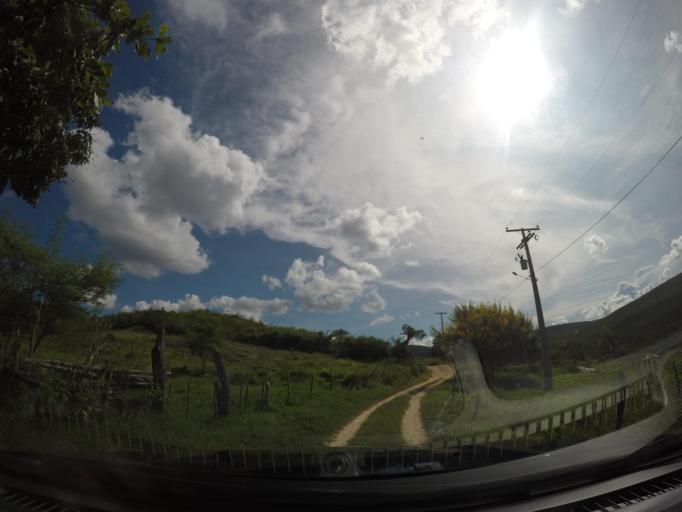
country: BR
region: Bahia
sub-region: Barra Da Estiva
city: Barra da Estiva
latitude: -13.1298
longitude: -41.5946
